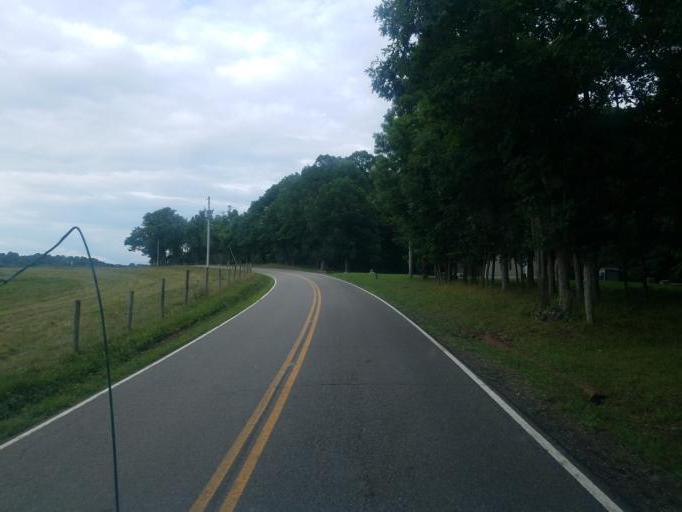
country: US
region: Ohio
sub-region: Knox County
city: Oak Hill
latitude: 40.4111
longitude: -82.1058
